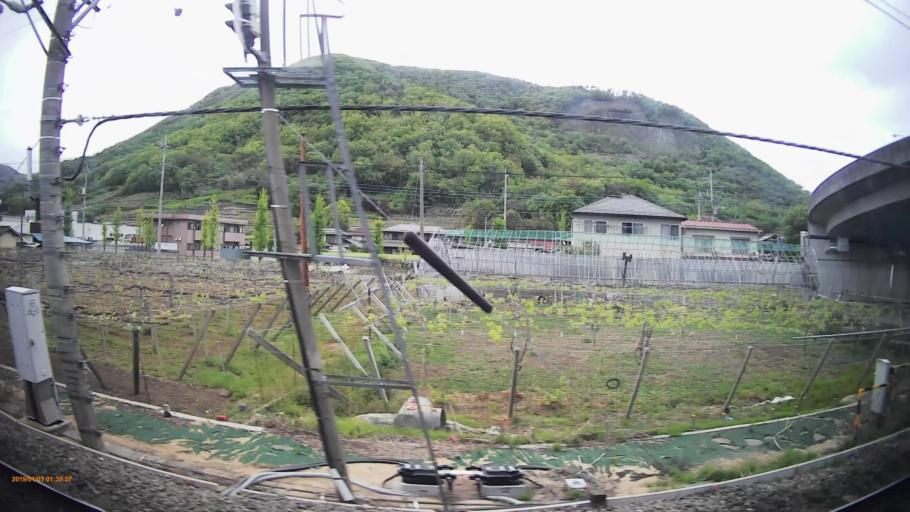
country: JP
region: Yamanashi
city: Isawa
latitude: 35.6575
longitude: 138.6301
